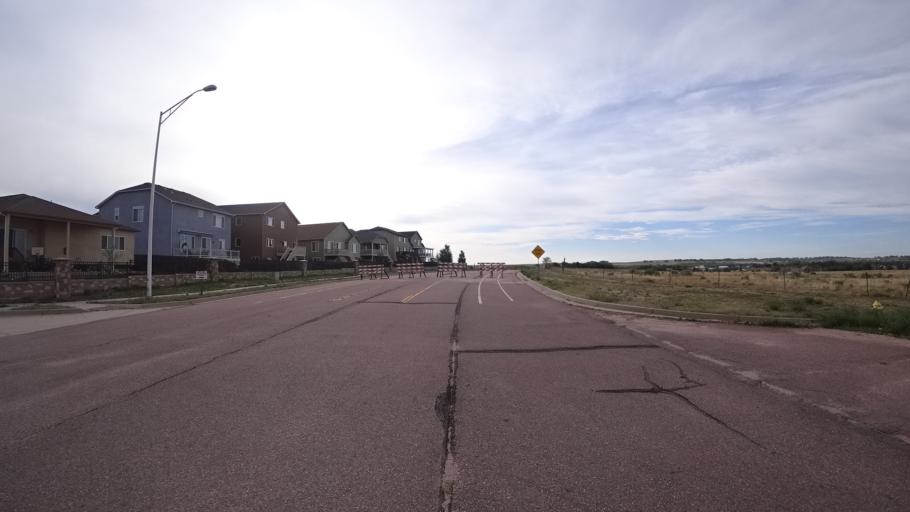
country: US
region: Colorado
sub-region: El Paso County
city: Fountain
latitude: 38.7152
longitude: -104.6837
